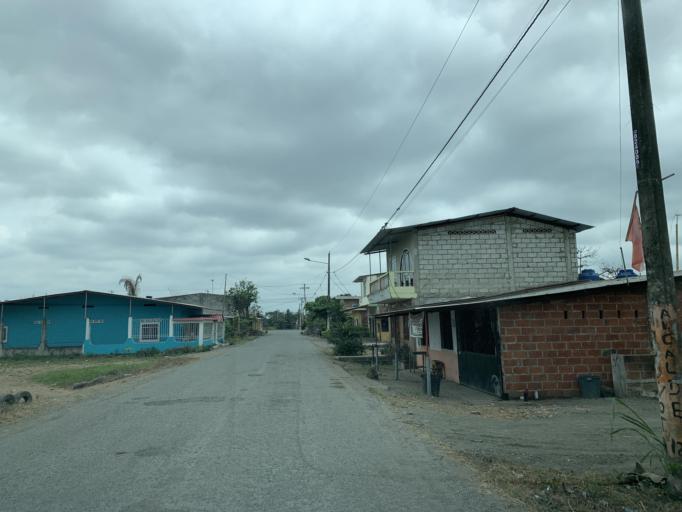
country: EC
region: Guayas
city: Coronel Marcelino Mariduena
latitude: -2.3177
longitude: -79.4697
